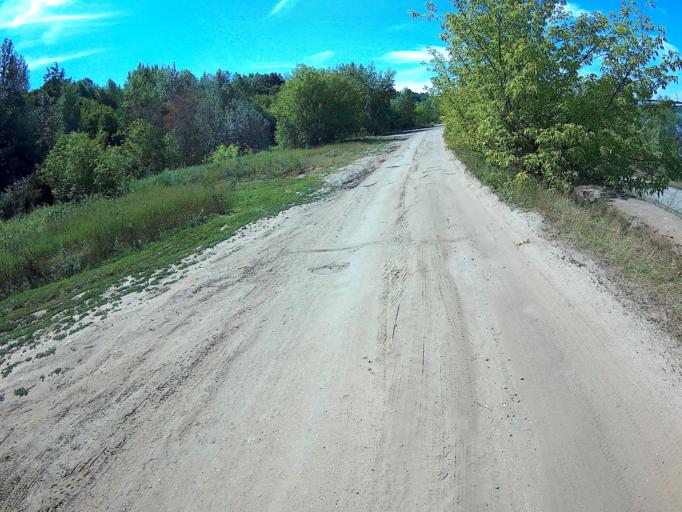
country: RU
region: Nizjnij Novgorod
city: Nizhniy Novgorod
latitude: 56.2577
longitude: 43.9646
